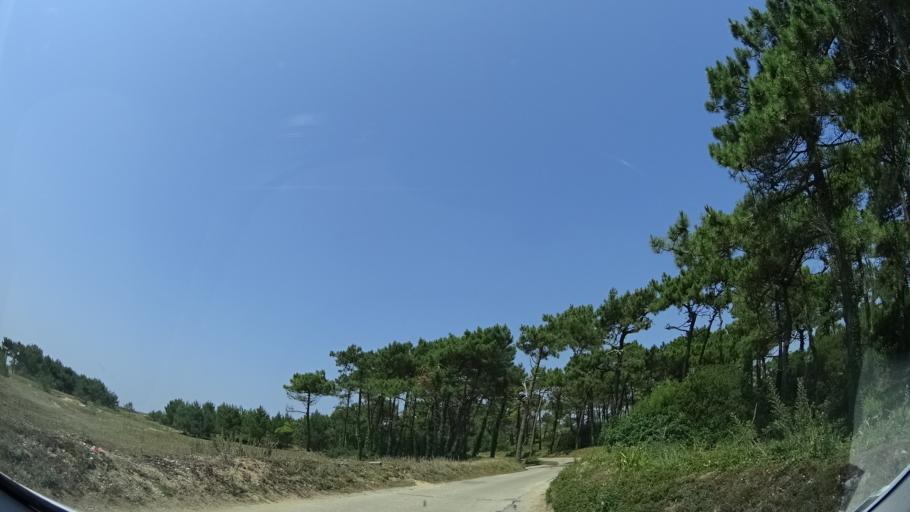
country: FR
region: Brittany
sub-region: Departement du Morbihan
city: Plouharnel
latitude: 47.5942
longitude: -3.1362
